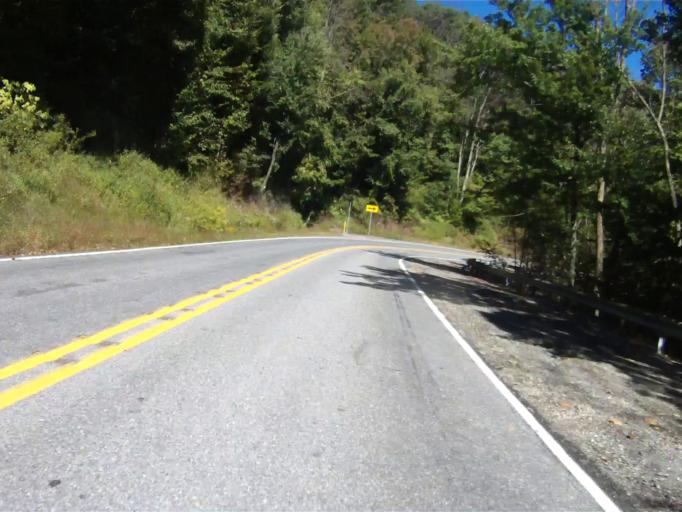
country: US
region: Pennsylvania
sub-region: Centre County
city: Park Forest Village
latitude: 40.9260
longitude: -77.9468
